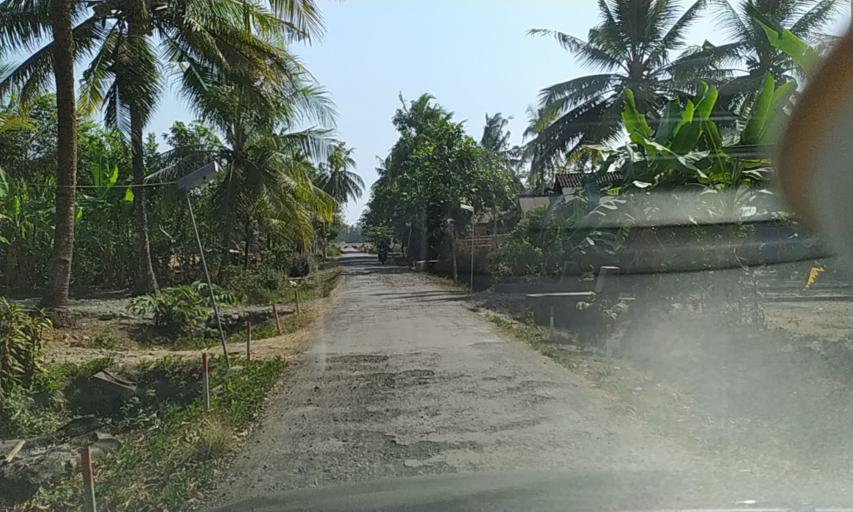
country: ID
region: Central Java
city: Ciklapa
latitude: -7.5074
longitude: 108.8028
